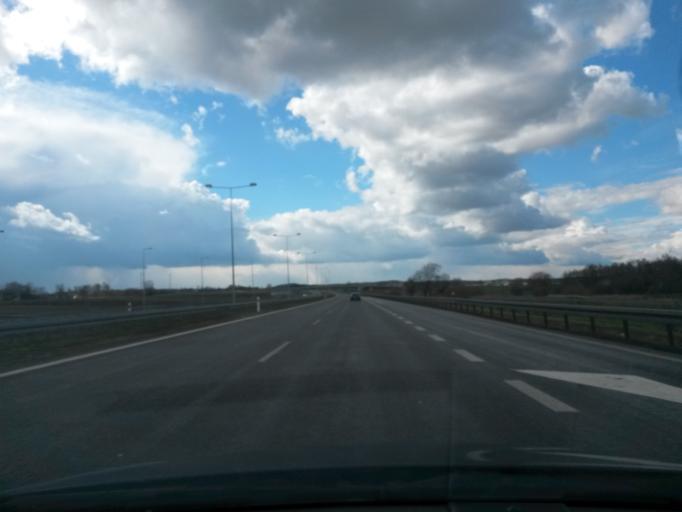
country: PL
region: Greater Poland Voivodeship
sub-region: Powiat turecki
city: Brudzew
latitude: 52.1409
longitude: 18.6067
